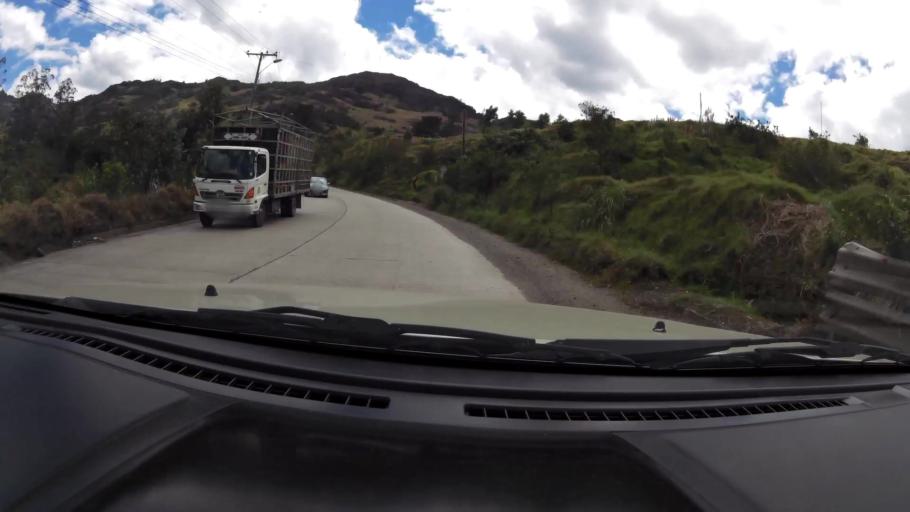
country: EC
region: Azuay
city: Cuenca
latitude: -3.1341
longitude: -79.1244
